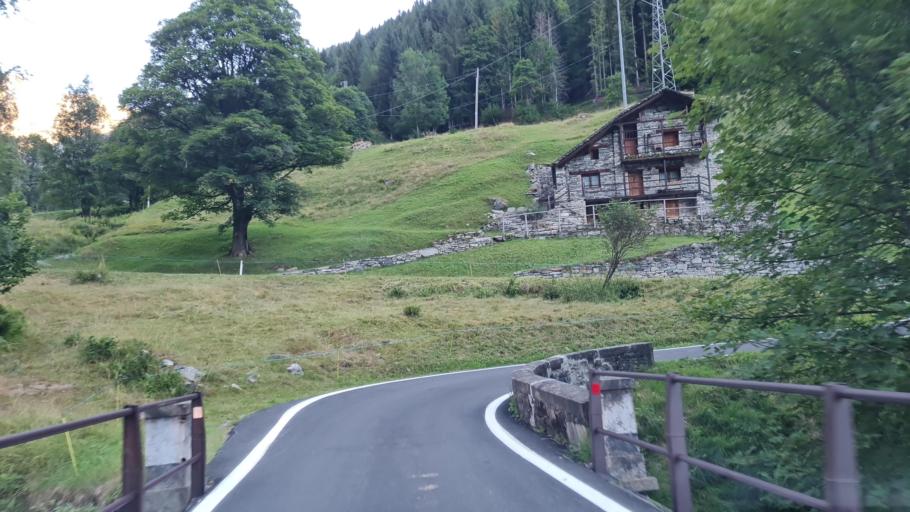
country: IT
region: Piedmont
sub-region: Provincia di Vercelli
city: Rima
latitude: 45.8799
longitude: 8.0091
